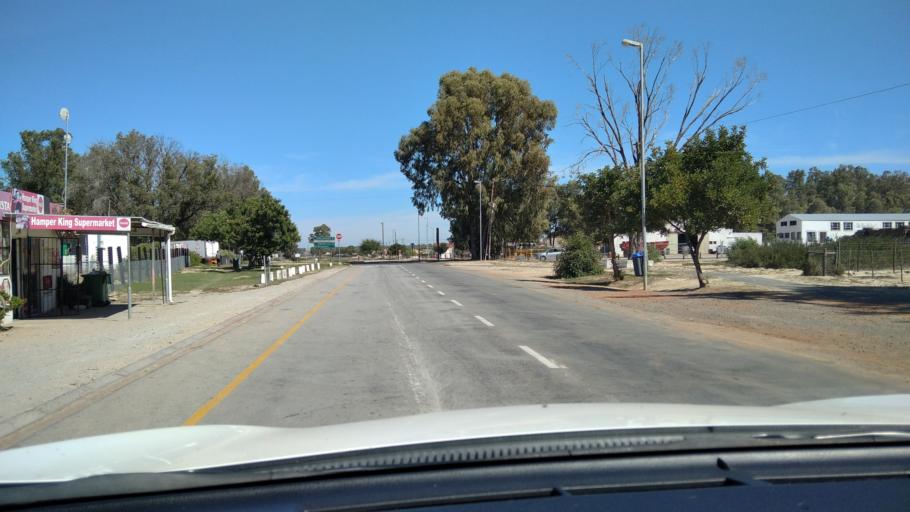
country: ZA
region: Western Cape
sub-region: West Coast District Municipality
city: Moorreesburg
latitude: -33.0591
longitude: 18.3420
